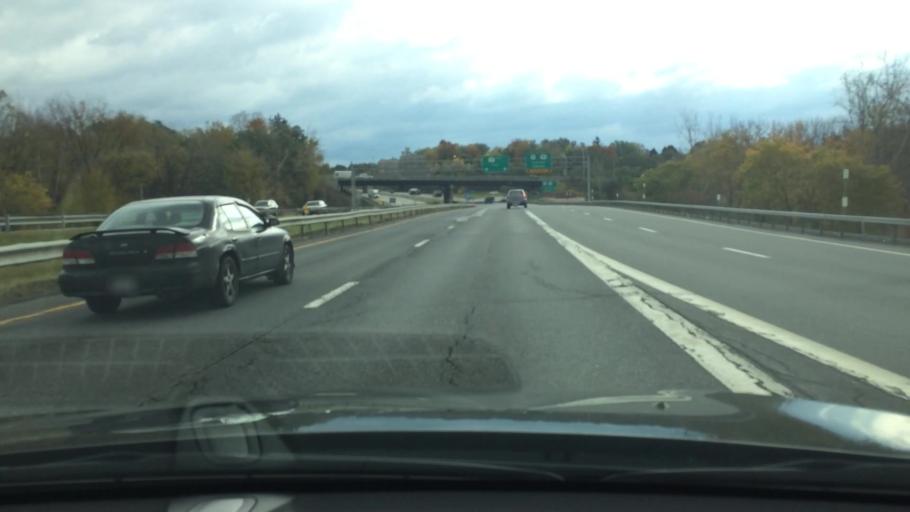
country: US
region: New York
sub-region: Albany County
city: Cohoes
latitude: 42.7617
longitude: -73.7599
